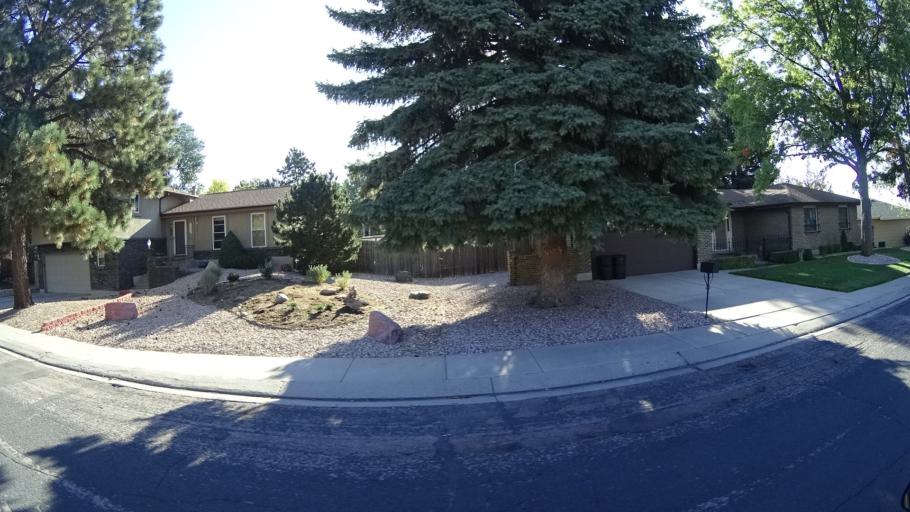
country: US
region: Colorado
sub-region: El Paso County
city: Cimarron Hills
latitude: 38.9073
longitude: -104.7538
